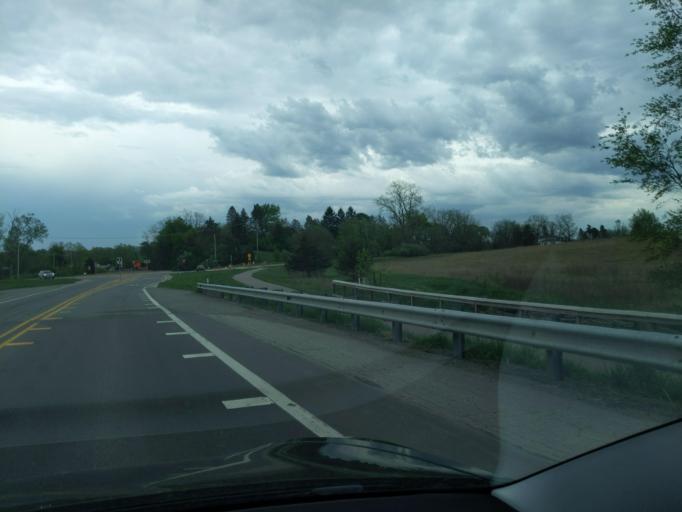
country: US
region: Michigan
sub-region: Washtenaw County
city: Chelsea
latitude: 42.3376
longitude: -84.0301
